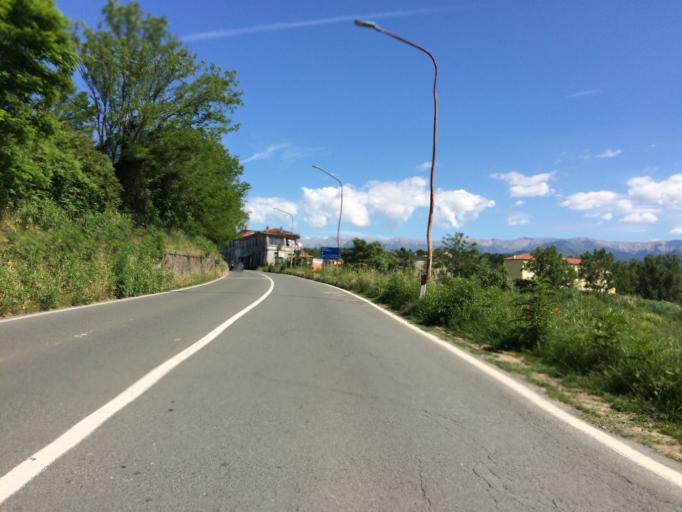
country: IT
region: Tuscany
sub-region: Provincia di Massa-Carrara
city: Terrarossa
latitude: 44.2216
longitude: 9.9700
